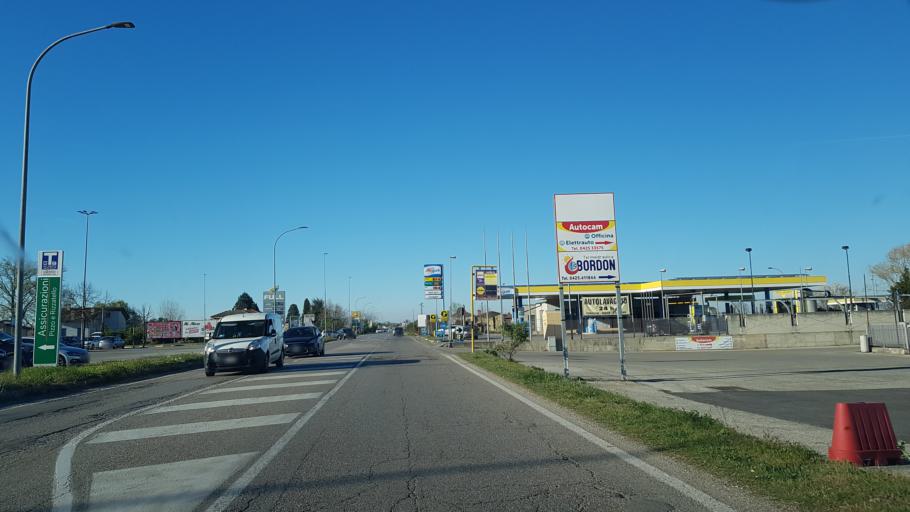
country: IT
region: Veneto
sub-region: Provincia di Rovigo
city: Rovigo
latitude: 45.0883
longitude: 11.7854
